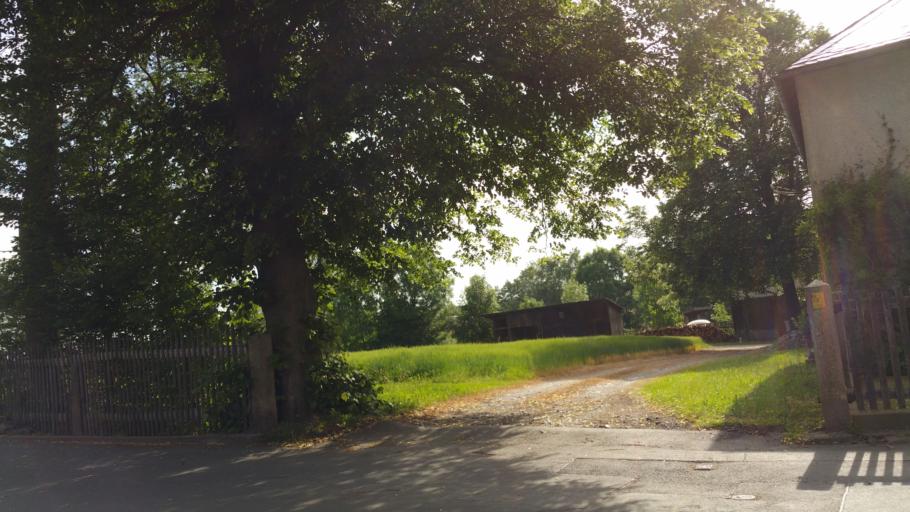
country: DE
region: Bavaria
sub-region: Upper Franconia
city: Schwarzenbach an der Saale
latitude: 50.2079
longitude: 11.9688
